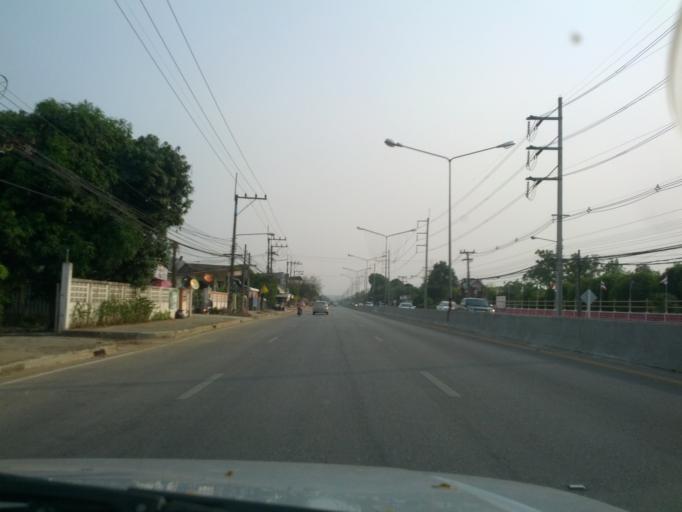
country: TH
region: Chiang Mai
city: Mae Taeng
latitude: 19.1203
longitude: 98.9425
